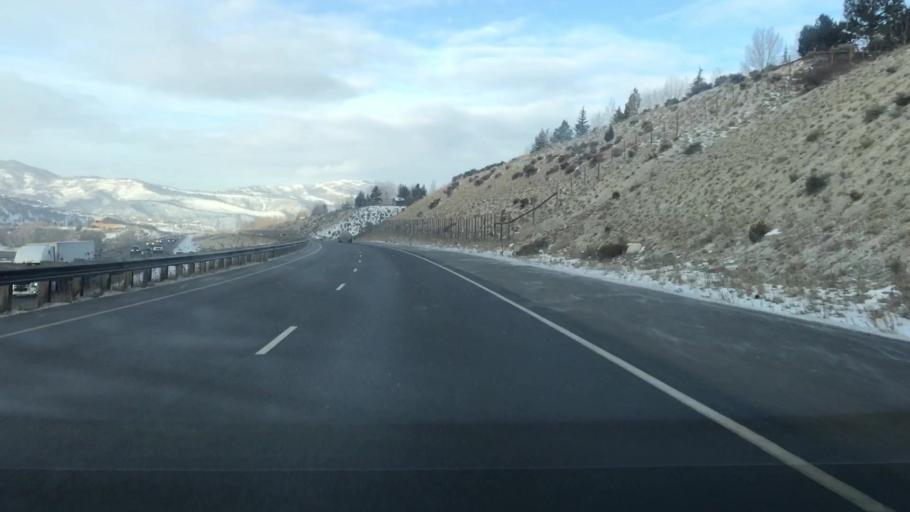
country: US
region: Colorado
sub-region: Eagle County
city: Edwards
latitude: 39.6428
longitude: -106.5574
